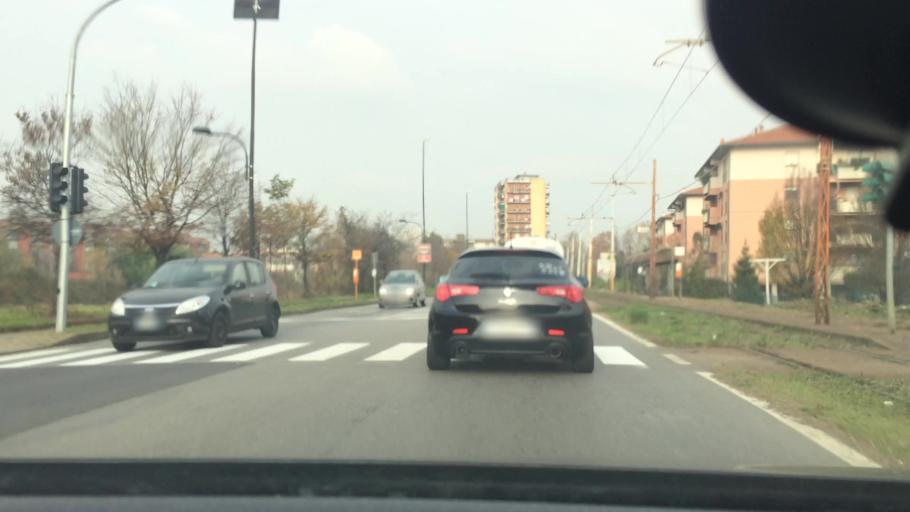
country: IT
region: Lombardy
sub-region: Provincia di Monza e Brianza
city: Villaggio del Sole
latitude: 45.6144
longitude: 9.1208
